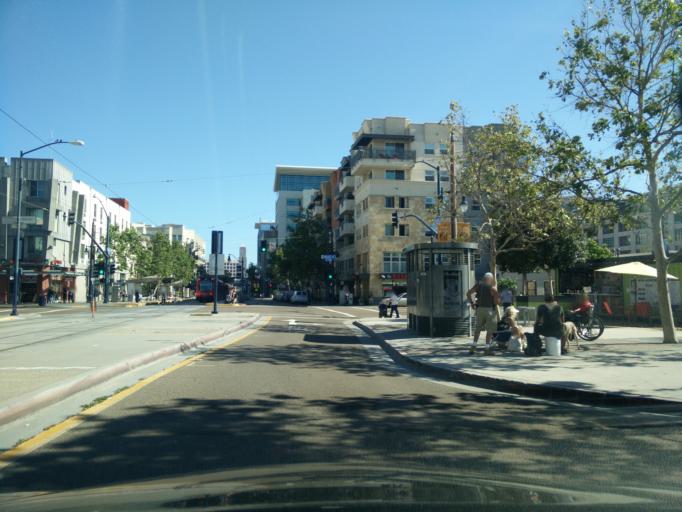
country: US
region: California
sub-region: San Diego County
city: San Diego
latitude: 32.7120
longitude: -117.1539
